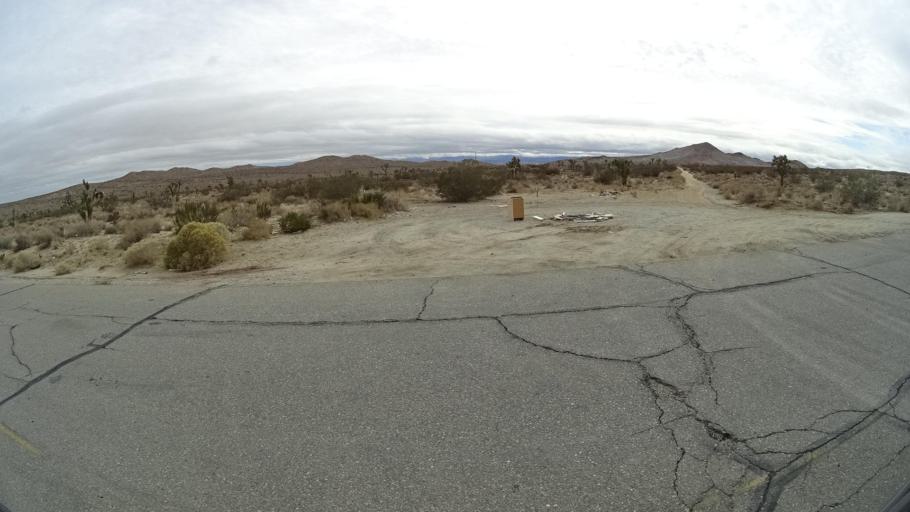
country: US
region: California
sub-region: Kern County
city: Rosamond
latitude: 34.9082
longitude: -118.1611
